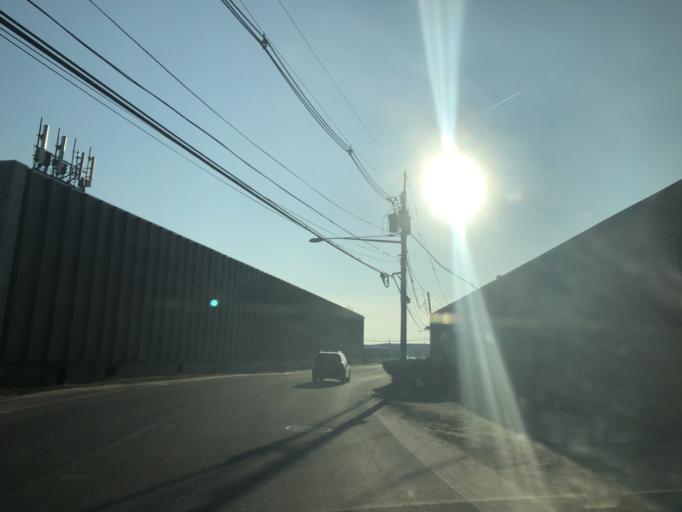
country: US
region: New Jersey
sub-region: Hudson County
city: Jersey City
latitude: 40.7026
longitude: -74.0644
